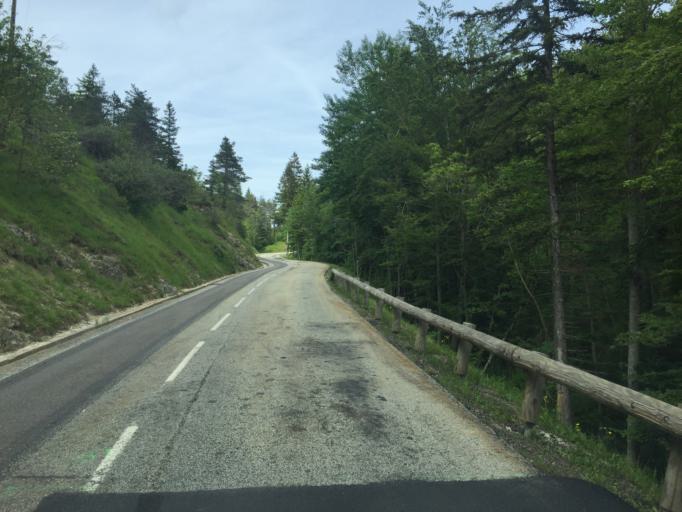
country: FR
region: Rhone-Alpes
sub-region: Departement de la Savoie
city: Saint-Baldoph
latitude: 45.4759
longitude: 5.9078
